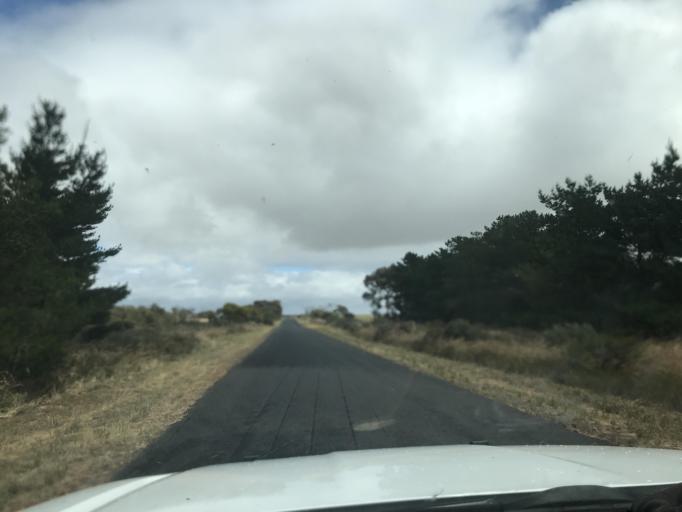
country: AU
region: South Australia
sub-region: Tatiara
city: Bordertown
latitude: -36.1358
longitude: 141.1881
